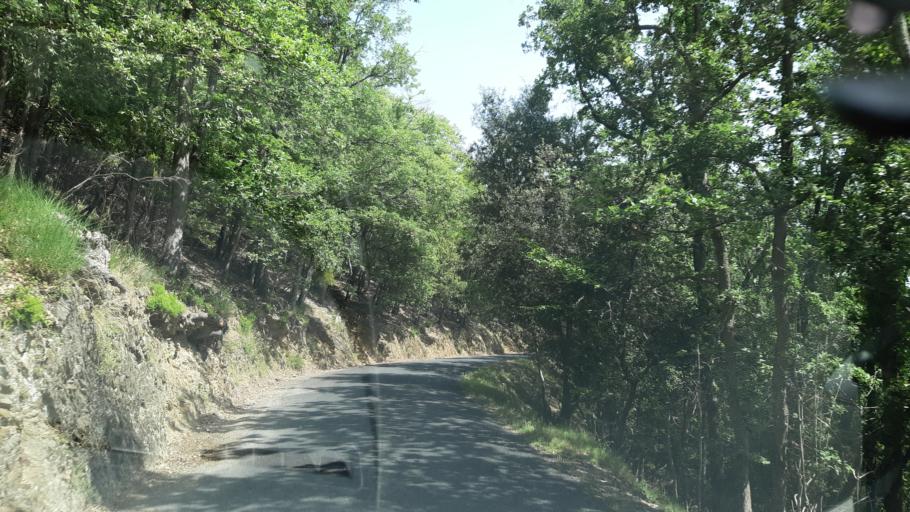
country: FR
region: Languedoc-Roussillon
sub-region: Departement des Pyrenees-Orientales
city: els Banys d'Arles
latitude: 42.5098
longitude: 2.6368
